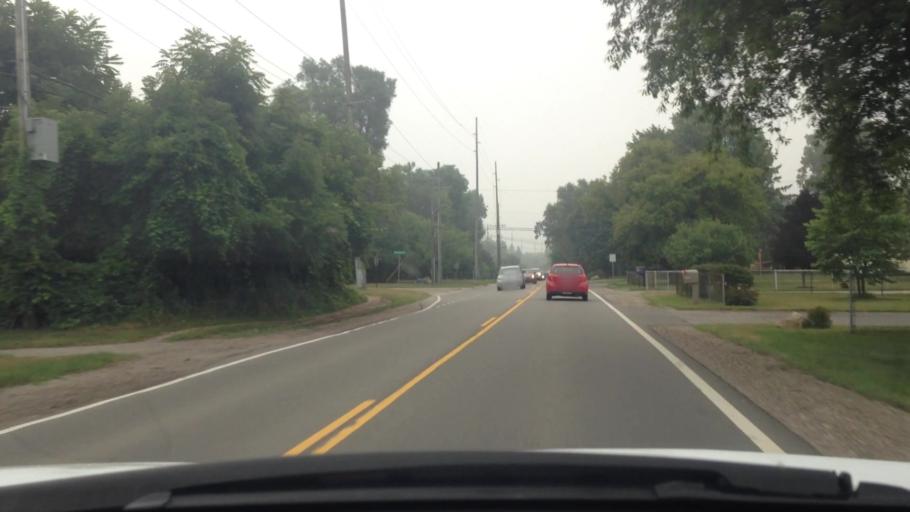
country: US
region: Michigan
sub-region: Oakland County
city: Waterford
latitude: 42.7017
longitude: -83.3488
